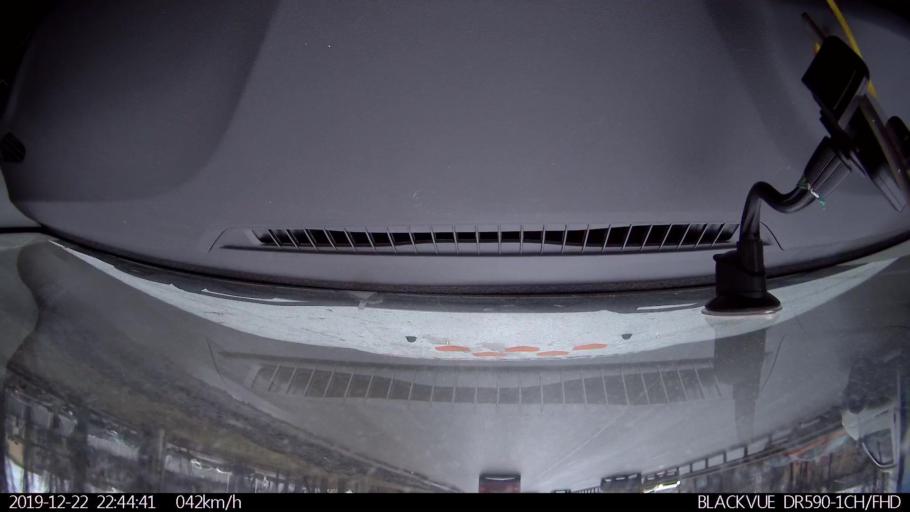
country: RU
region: Nizjnij Novgorod
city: Nizhniy Novgorod
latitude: 56.2719
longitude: 43.9093
